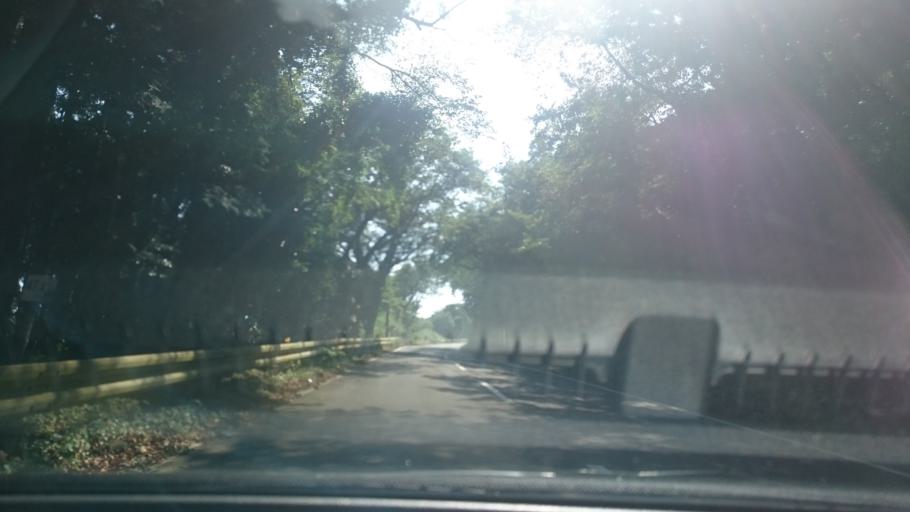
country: JP
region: Shizuoka
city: Heda
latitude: 34.9522
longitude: 138.7757
